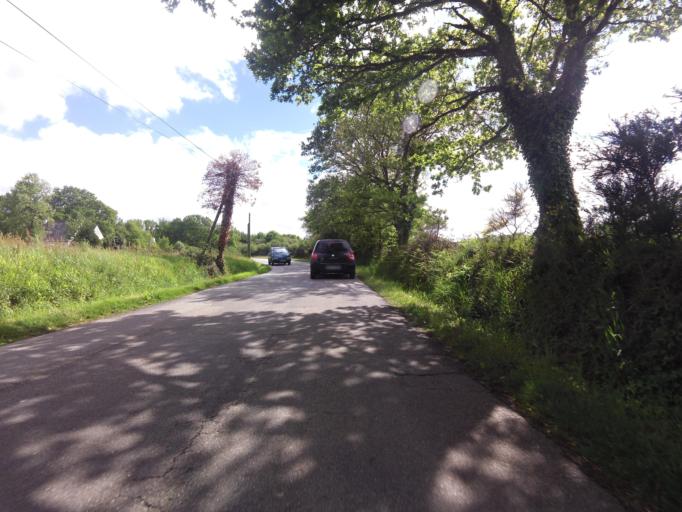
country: FR
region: Brittany
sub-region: Departement du Morbihan
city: Plougoumelen
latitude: 47.6381
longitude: -2.9258
